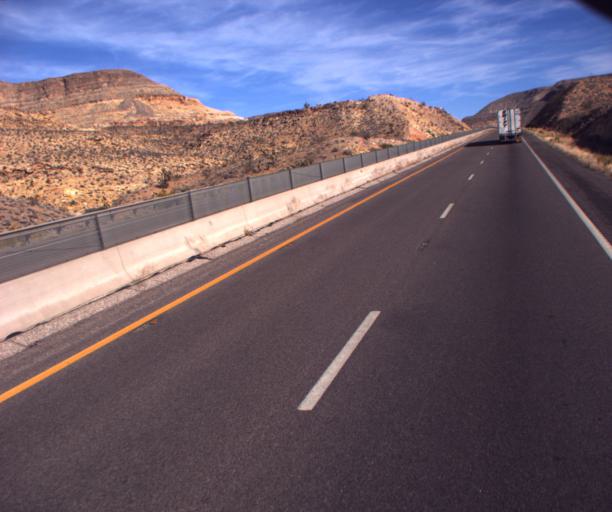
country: US
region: Utah
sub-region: Washington County
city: Santa Clara
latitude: 36.9711
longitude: -113.7488
